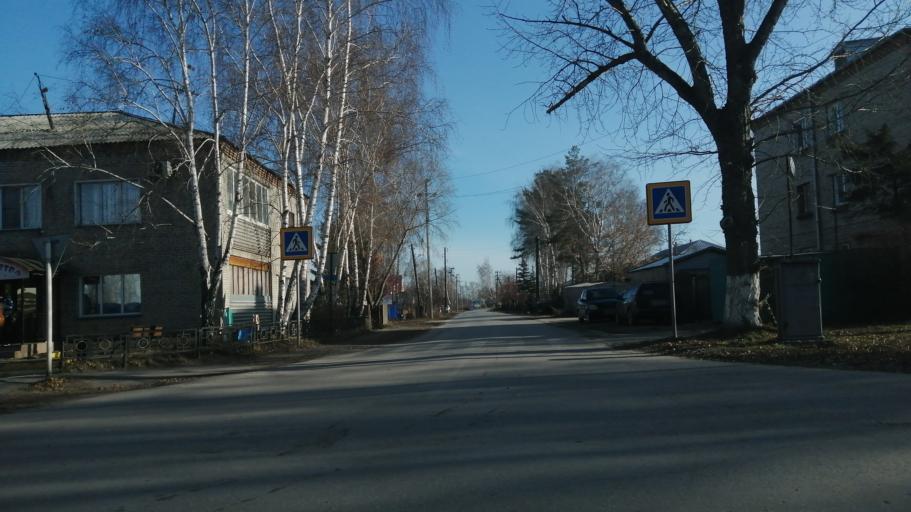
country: RU
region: Novosibirsk
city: Krasnozerskoye
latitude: 53.9820
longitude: 79.2412
